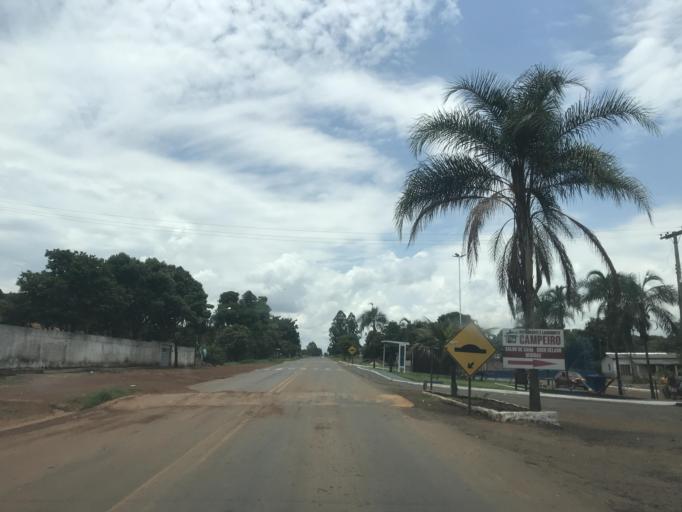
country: BR
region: Goias
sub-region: Vianopolis
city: Vianopolis
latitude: -16.7247
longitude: -48.4324
